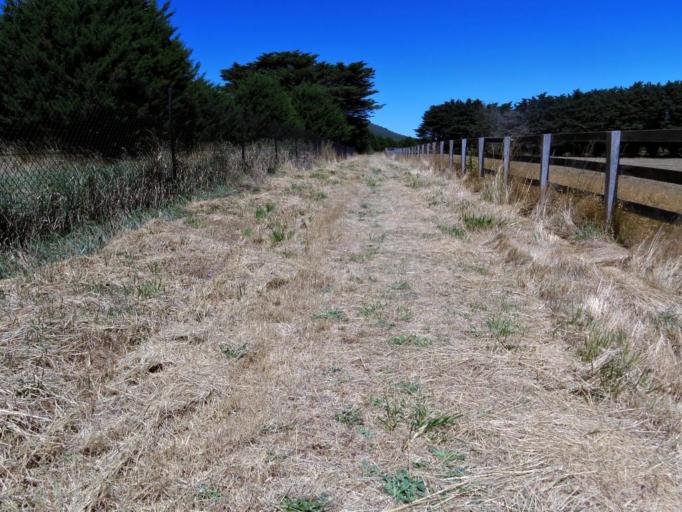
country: AU
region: Victoria
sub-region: Hume
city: Sunbury
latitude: -37.3509
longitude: 144.5491
